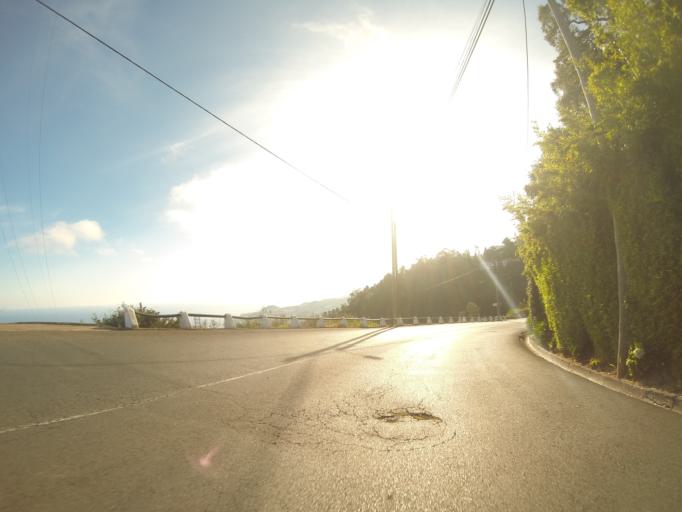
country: PT
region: Madeira
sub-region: Funchal
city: Nossa Senhora do Monte
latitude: 32.6636
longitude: -16.8711
